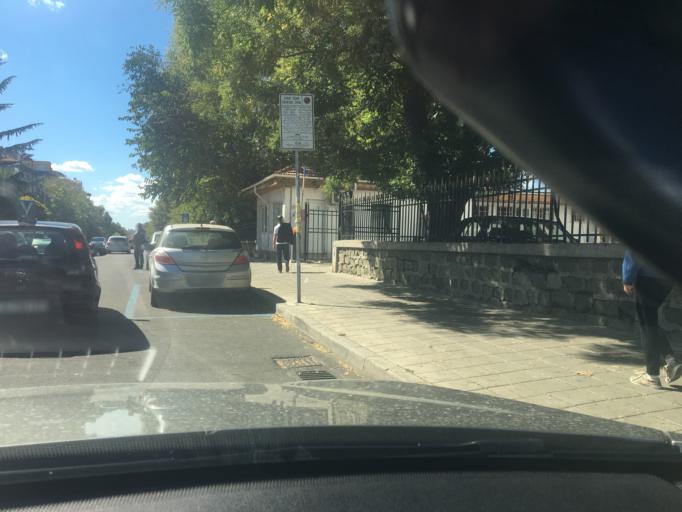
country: BG
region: Burgas
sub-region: Obshtina Burgas
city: Burgas
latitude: 42.5006
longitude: 27.4773
